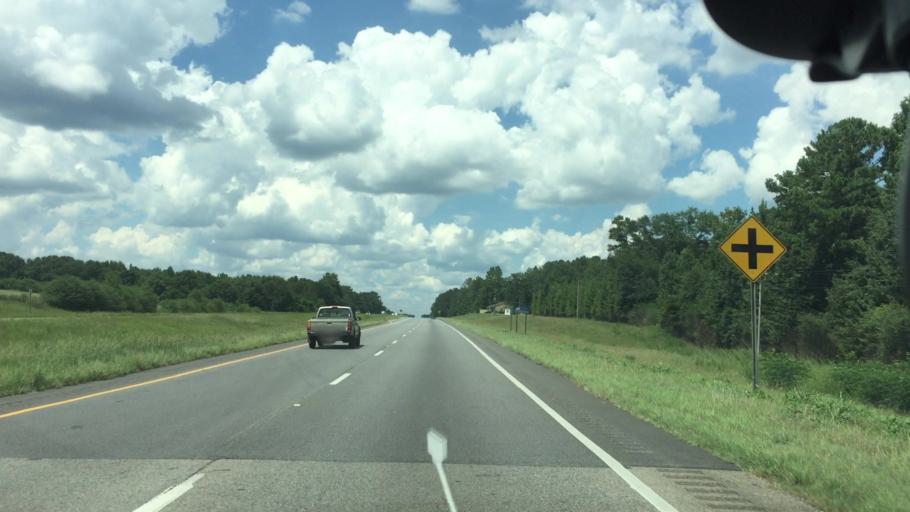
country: US
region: Alabama
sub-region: Pike County
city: Troy
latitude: 31.8727
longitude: -86.0016
